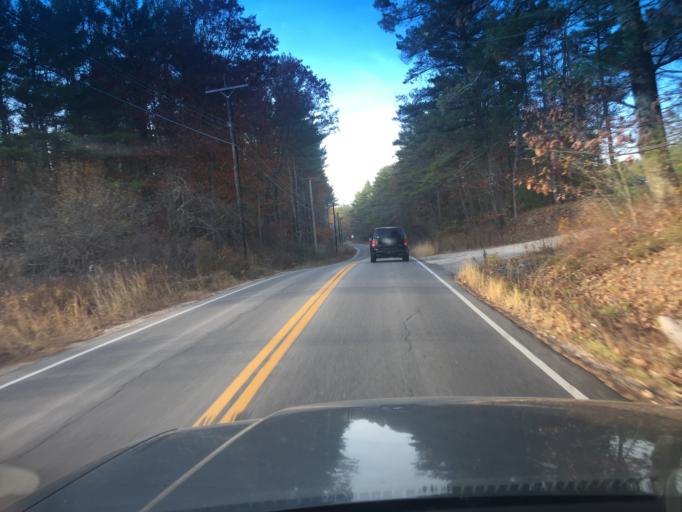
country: US
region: Maine
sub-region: York County
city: York Harbor
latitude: 43.1708
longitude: -70.7163
